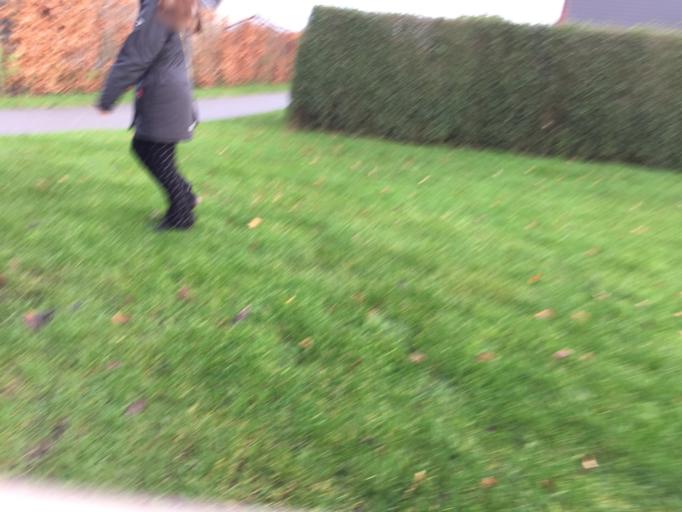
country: DK
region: Central Jutland
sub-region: Ringkobing-Skjern Kommune
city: Ringkobing
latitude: 56.0933
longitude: 8.2715
